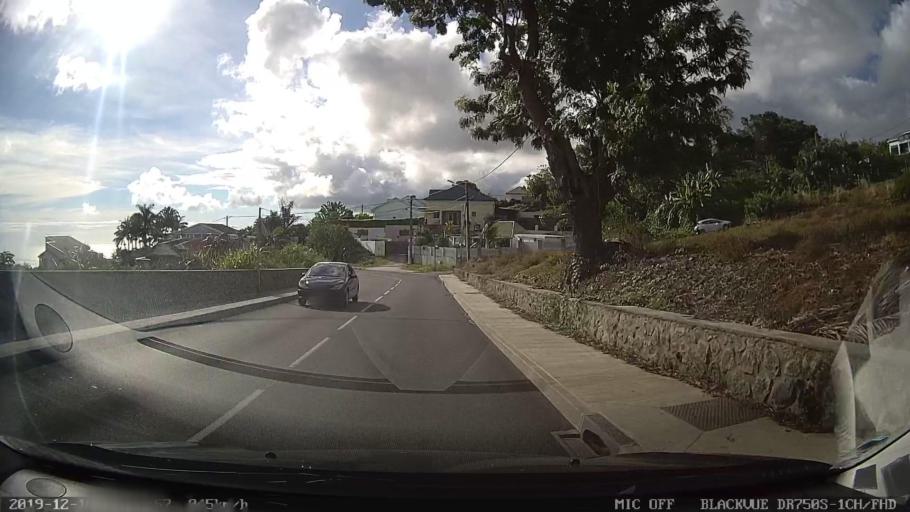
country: RE
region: Reunion
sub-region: Reunion
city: Le Tampon
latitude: -21.2454
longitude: 55.5149
